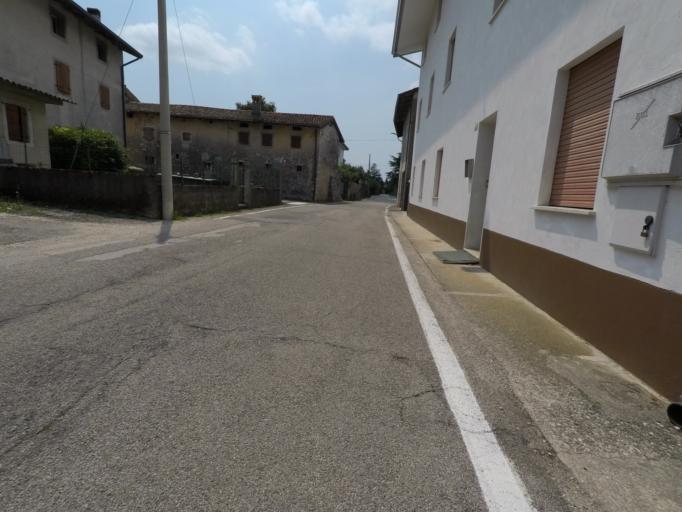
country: IT
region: Friuli Venezia Giulia
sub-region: Provincia di Pordenone
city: Aviano-Castello
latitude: 46.0578
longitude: 12.5753
